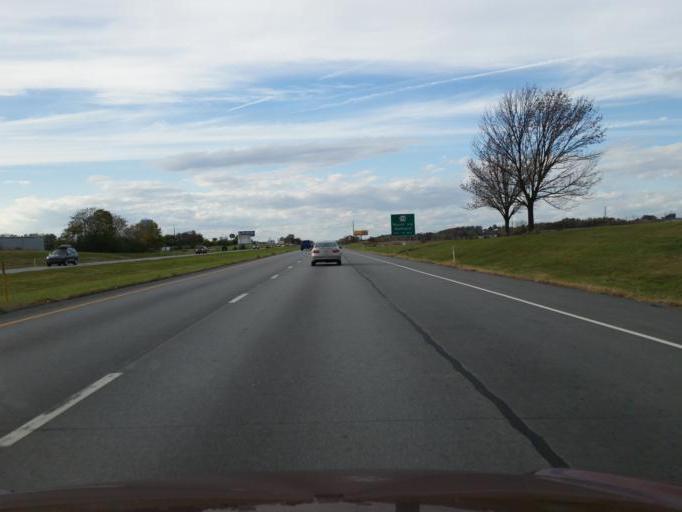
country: US
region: Pennsylvania
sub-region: Lancaster County
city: Salunga
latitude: 40.1176
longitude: -76.4552
